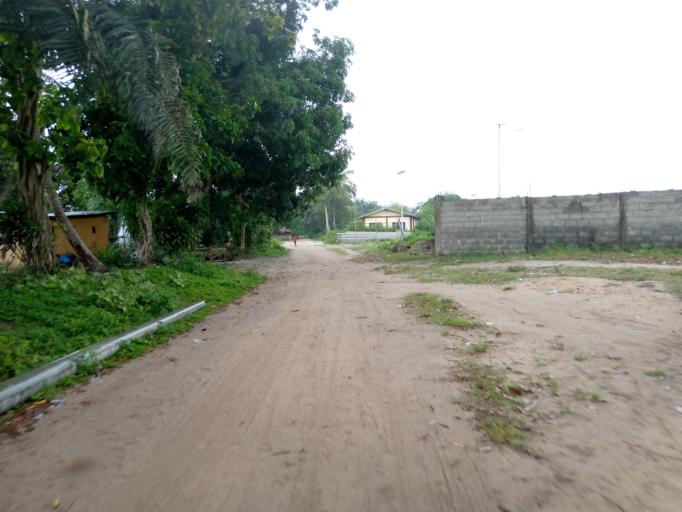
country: SL
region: Southern Province
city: Bonthe
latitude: 7.5288
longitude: -12.5080
